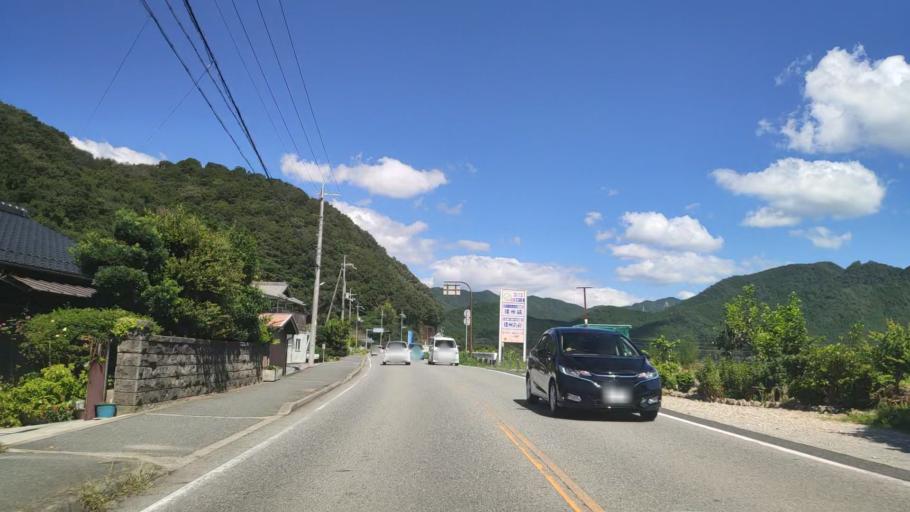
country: JP
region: Hyogo
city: Nishiwaki
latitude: 35.0675
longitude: 135.0090
